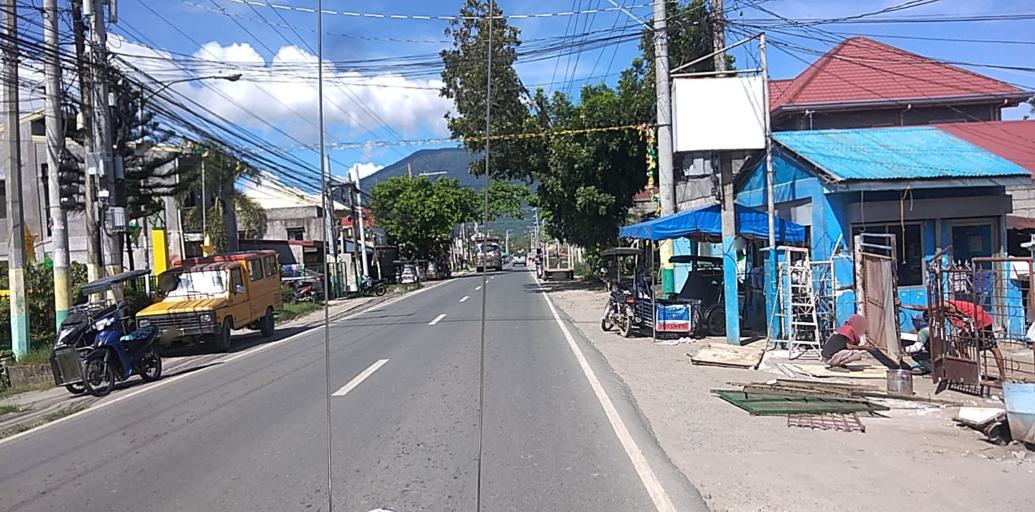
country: PH
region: Central Luzon
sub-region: Province of Pampanga
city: Arayat
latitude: 15.1416
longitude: 120.7722
